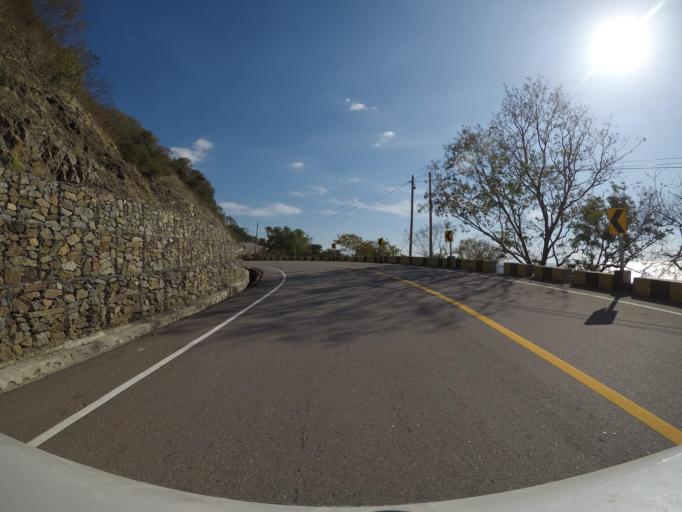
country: TL
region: Liquica
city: Maubara
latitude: -8.6489
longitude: 125.1224
